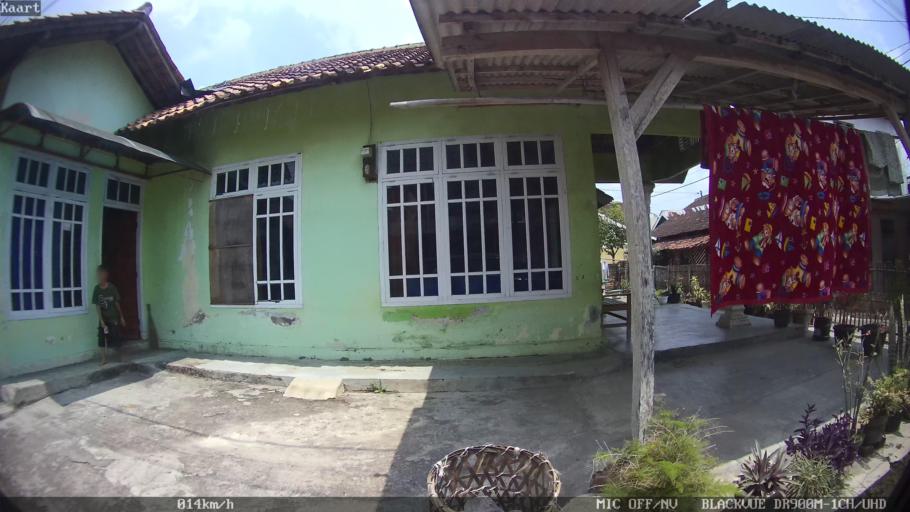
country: ID
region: Lampung
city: Pringsewu
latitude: -5.3571
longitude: 104.9880
